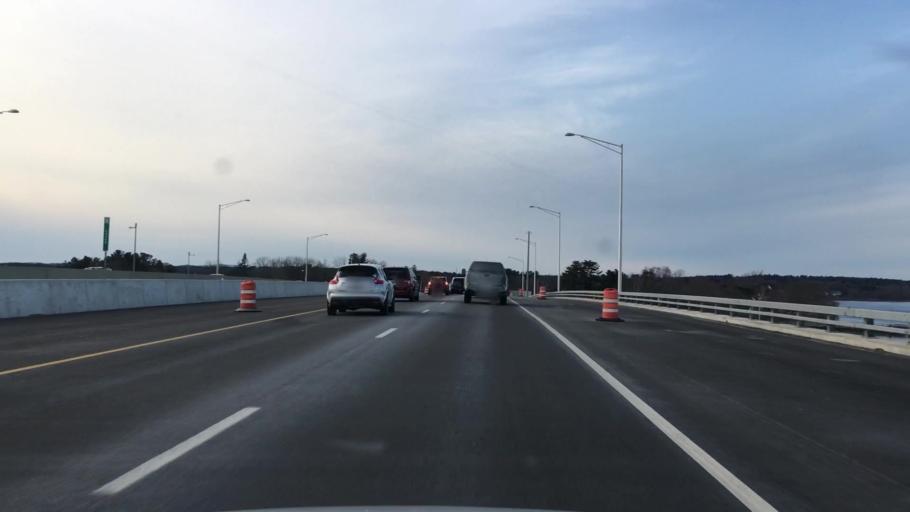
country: US
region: Maine
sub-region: York County
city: Eliot
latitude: 43.1181
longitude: -70.8255
